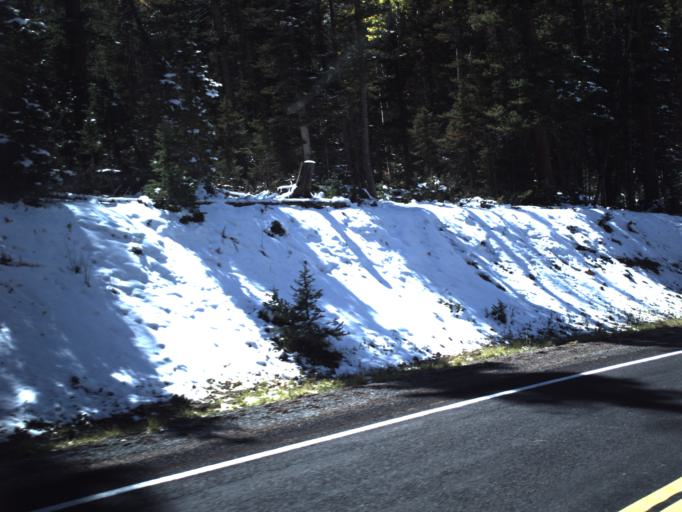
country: US
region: Utah
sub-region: Piute County
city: Junction
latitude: 38.3065
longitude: -112.4106
